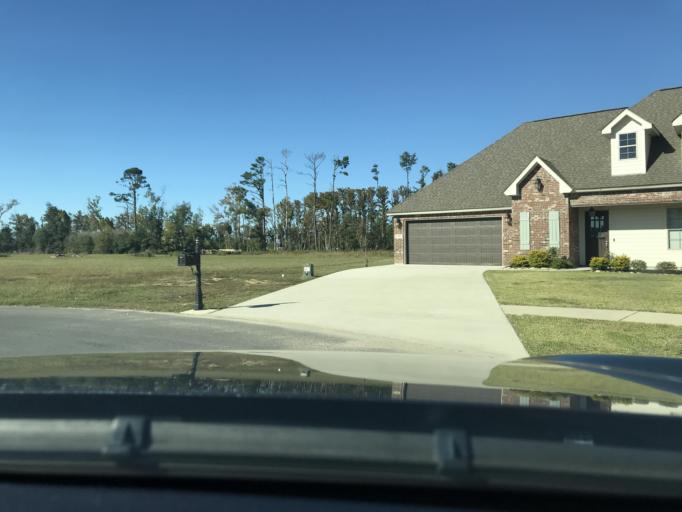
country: US
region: Louisiana
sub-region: Calcasieu Parish
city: Moss Bluff
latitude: 30.3139
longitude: -93.2564
